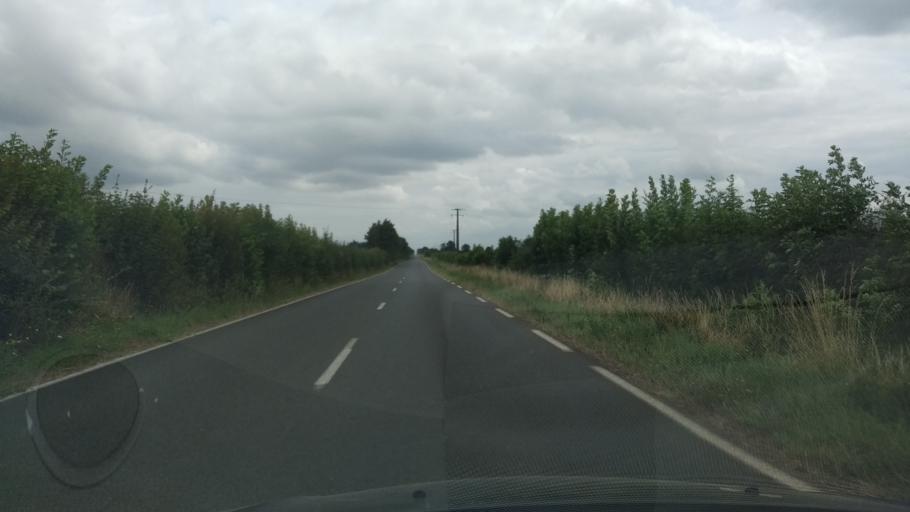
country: FR
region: Poitou-Charentes
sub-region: Departement de la Vienne
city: La Villedieu-du-Clain
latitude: 46.4249
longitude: 0.3797
